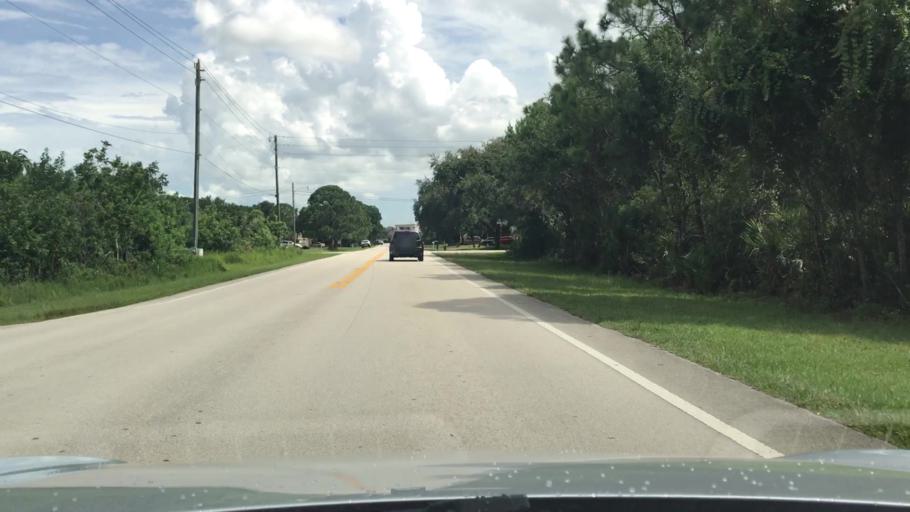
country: US
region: Florida
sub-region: Indian River County
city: Sebastian
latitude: 27.7828
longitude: -80.4975
